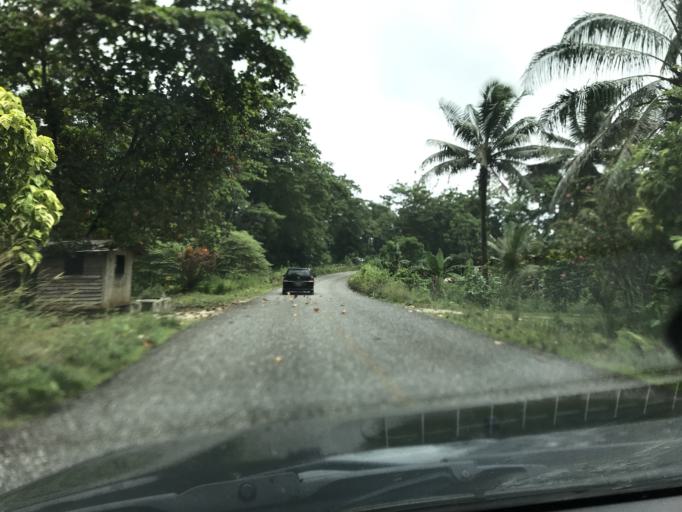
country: SB
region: Western Province
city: Gizo
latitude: -8.2331
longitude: 157.2130
